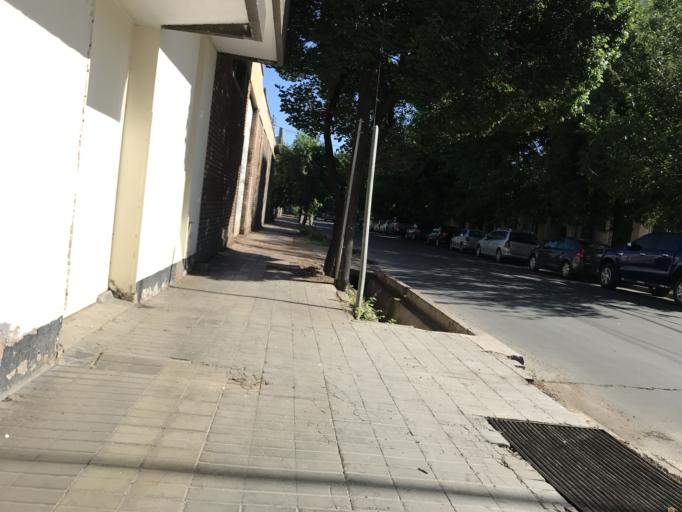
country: AR
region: Mendoza
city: Mendoza
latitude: -32.8849
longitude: -68.8312
